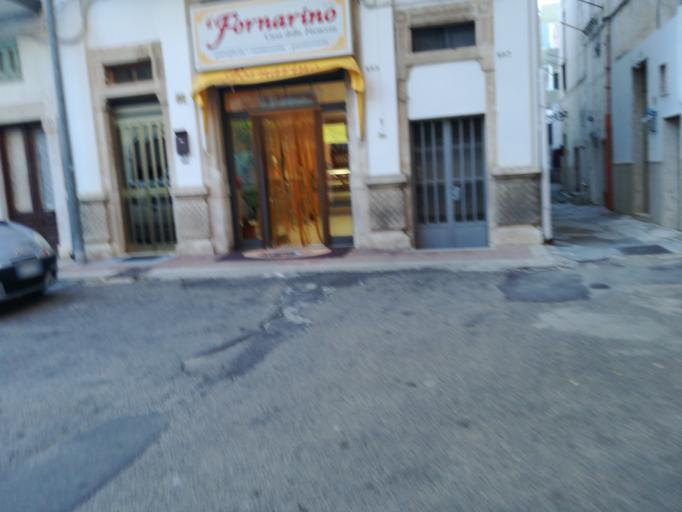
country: IT
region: Apulia
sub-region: Provincia di Bari
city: Triggiano
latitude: 41.0658
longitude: 16.9278
